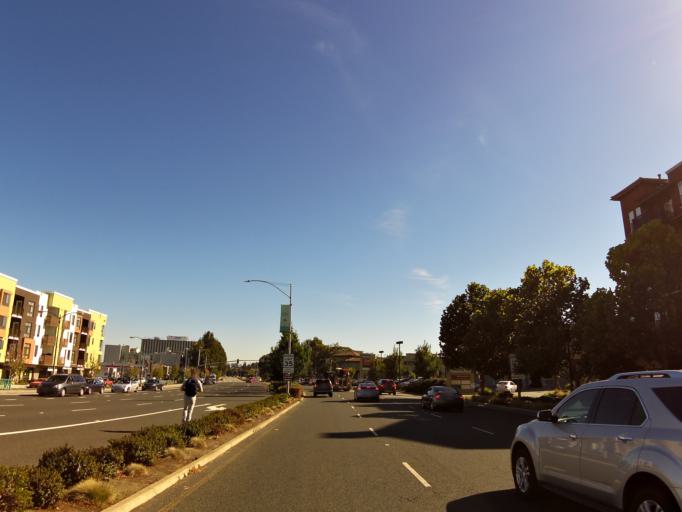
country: US
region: California
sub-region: San Mateo County
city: Millbrae
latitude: 37.5979
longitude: -122.3870
